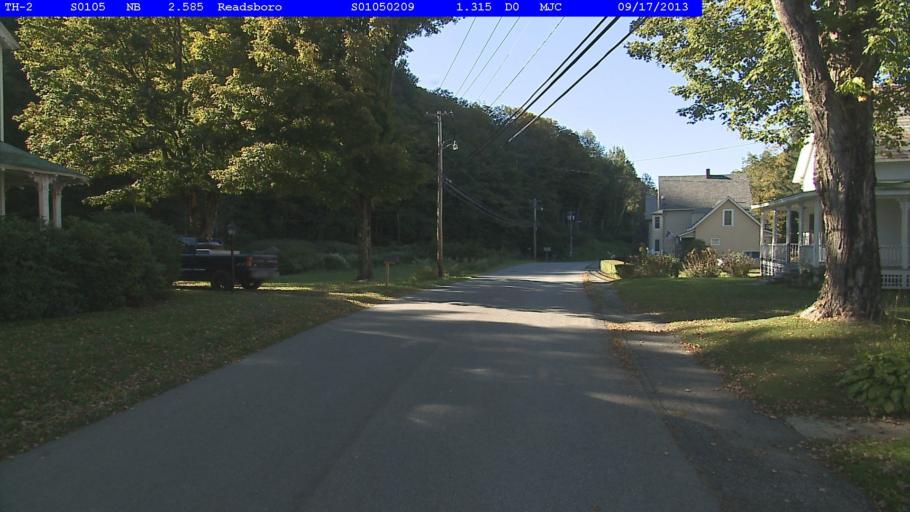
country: US
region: Massachusetts
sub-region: Franklin County
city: Charlemont
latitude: 42.7682
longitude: -72.9469
